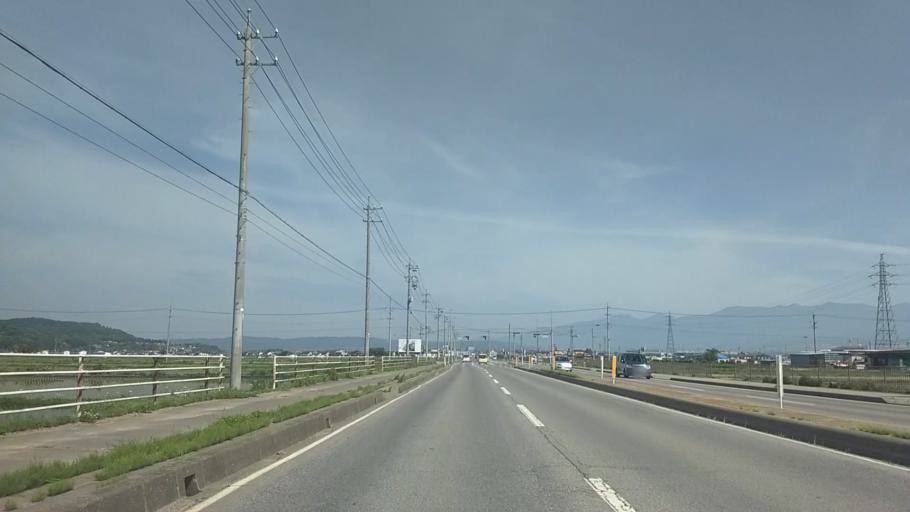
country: JP
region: Nagano
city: Saku
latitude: 36.2169
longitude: 138.4617
